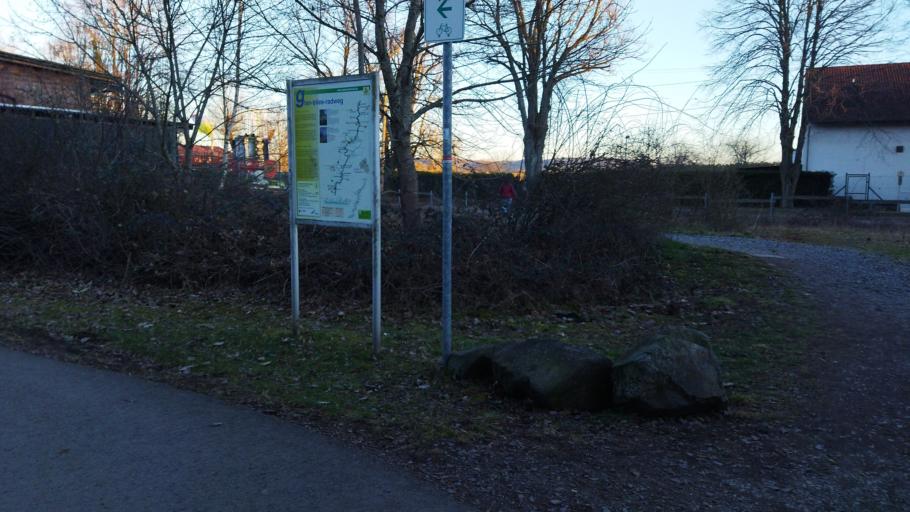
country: DE
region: Rheinland-Pfalz
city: Schonenberg-Kubelberg
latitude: 49.4045
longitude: 7.3744
